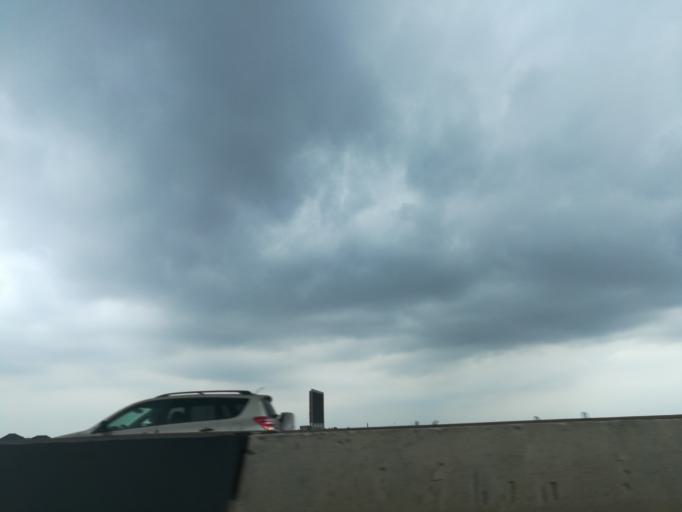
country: NG
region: Lagos
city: Somolu
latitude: 6.5322
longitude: 3.4016
